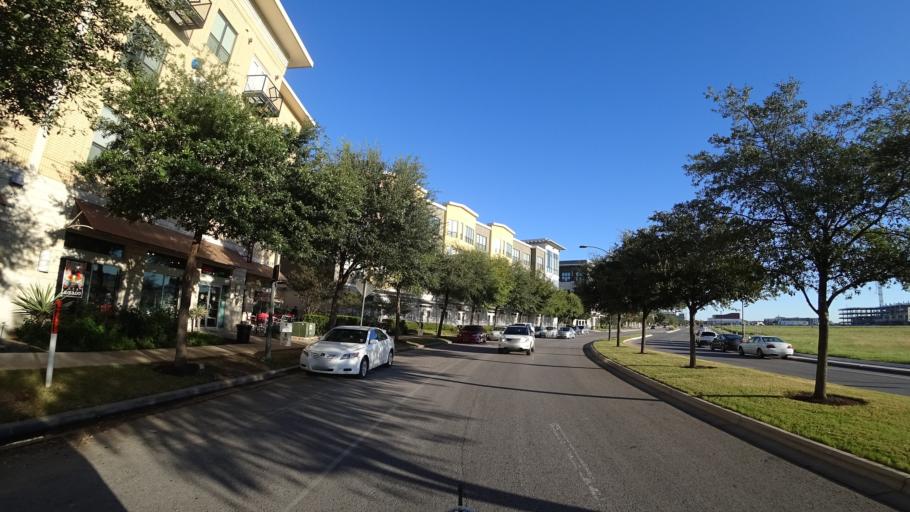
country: US
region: Texas
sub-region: Travis County
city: Austin
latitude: 30.2985
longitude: -97.7073
